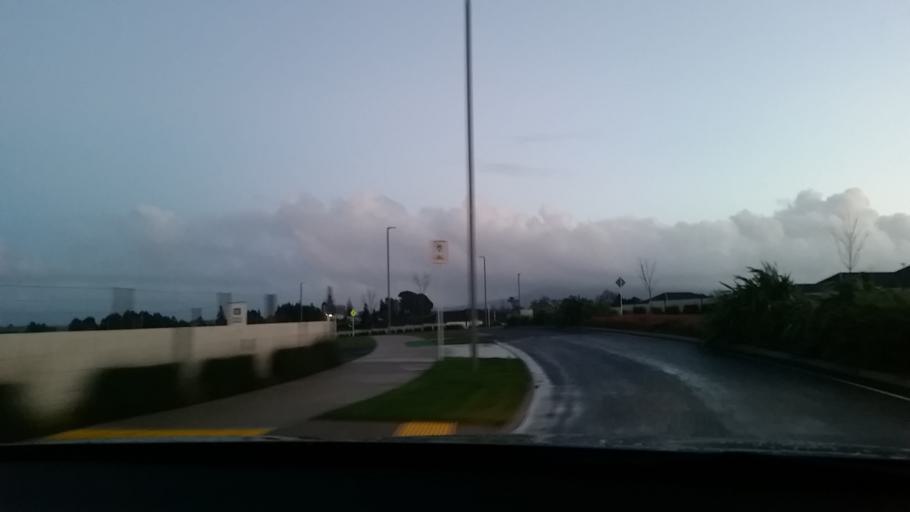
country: NZ
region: Waikato
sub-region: Hamilton City
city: Hamilton
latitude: -37.8183
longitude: 175.2266
